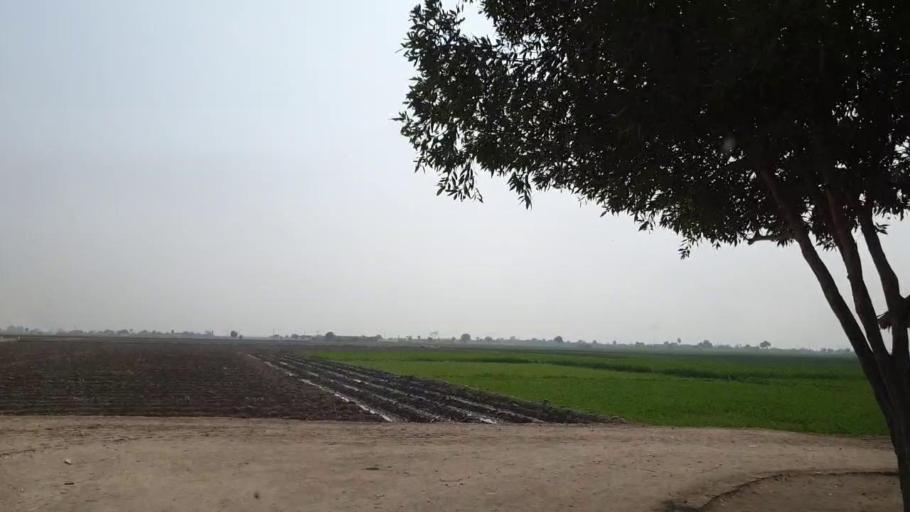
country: PK
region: Sindh
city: Mirpur Khas
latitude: 25.5469
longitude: 69.0914
